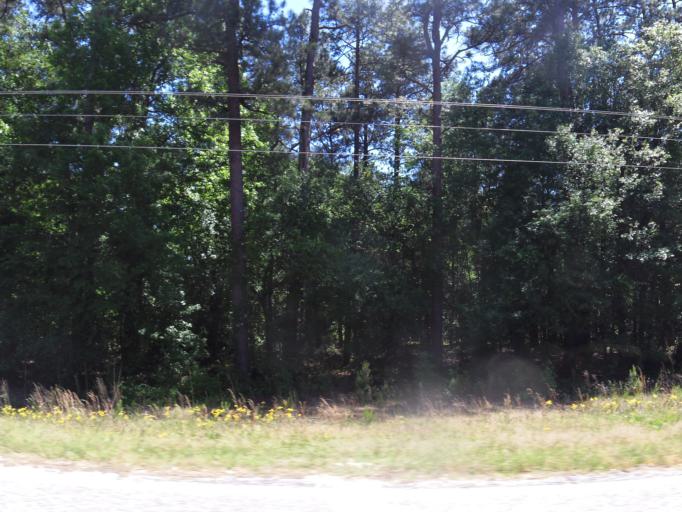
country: US
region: South Carolina
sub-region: Aiken County
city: Clearwater
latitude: 33.5080
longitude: -81.8807
